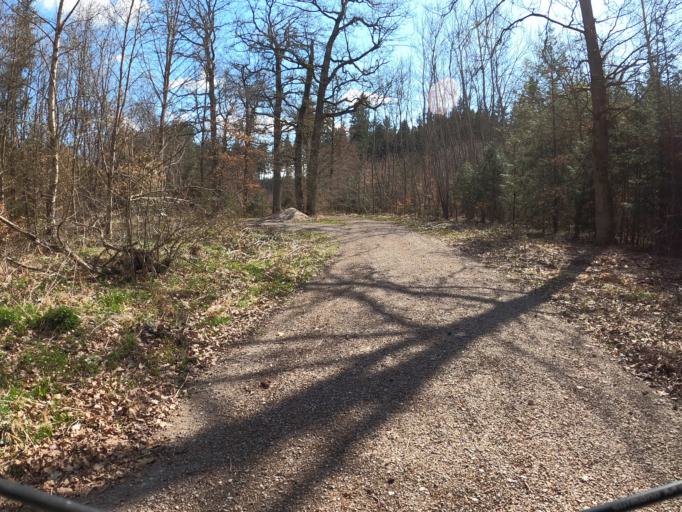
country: DE
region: Bavaria
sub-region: Swabia
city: Nersingen
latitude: 48.4019
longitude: 10.1539
